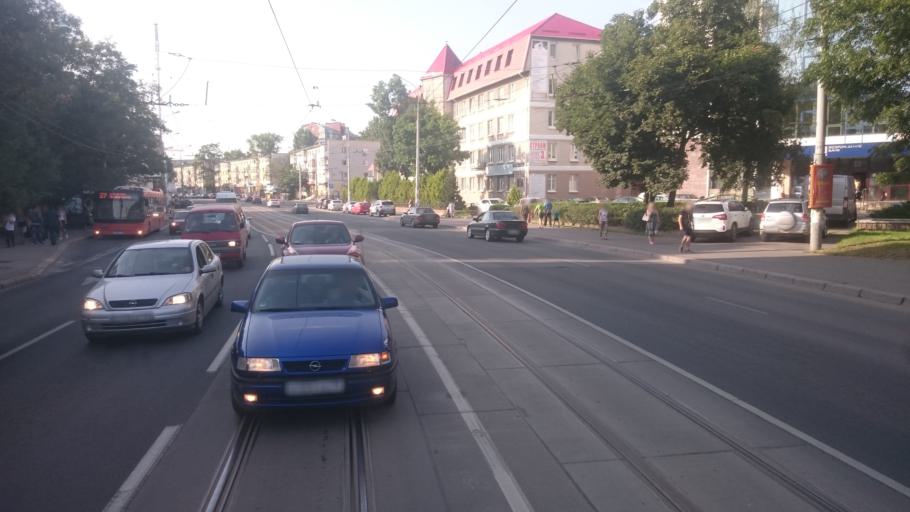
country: RU
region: Kaliningrad
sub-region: Gorod Kaliningrad
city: Kaliningrad
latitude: 54.7231
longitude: 20.4990
